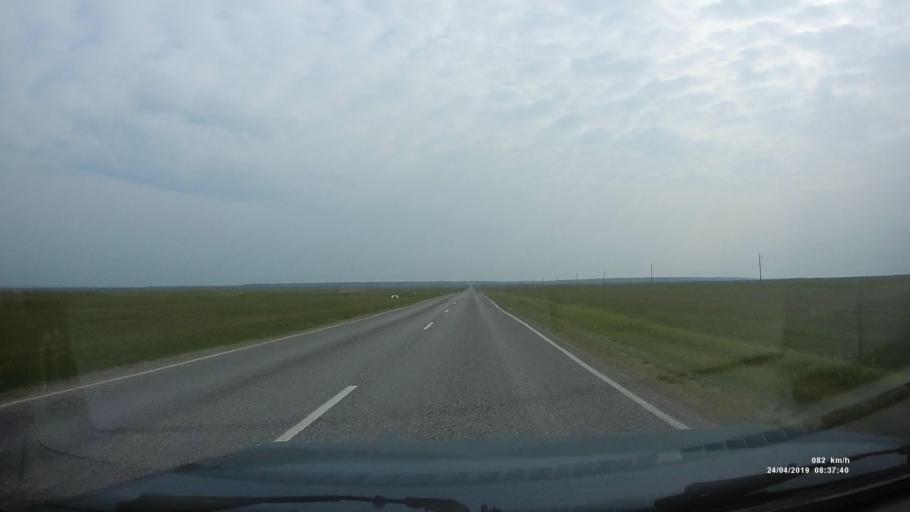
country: RU
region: Kalmykiya
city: Arshan'
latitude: 46.2113
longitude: 43.9546
